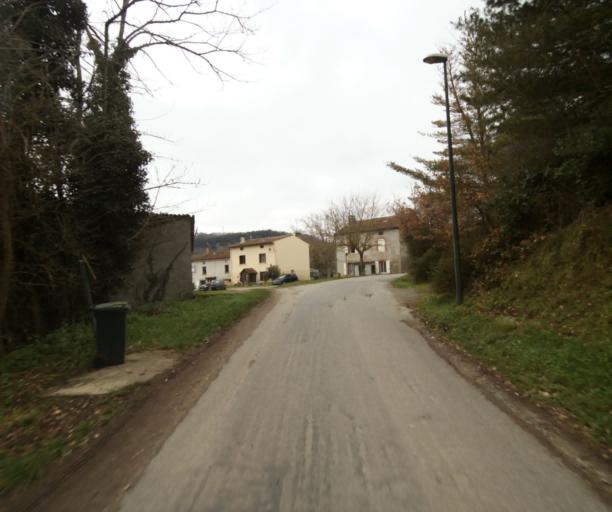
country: FR
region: Midi-Pyrenees
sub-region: Departement de l'Ariege
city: Pamiers
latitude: 43.1676
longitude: 1.5968
